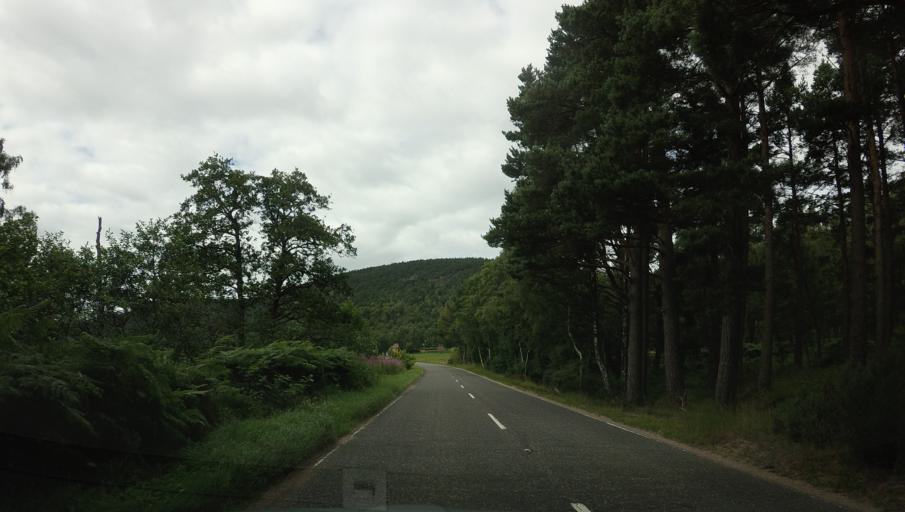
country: GB
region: Scotland
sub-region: Aberdeenshire
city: Ballater
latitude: 57.0573
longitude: -3.1142
